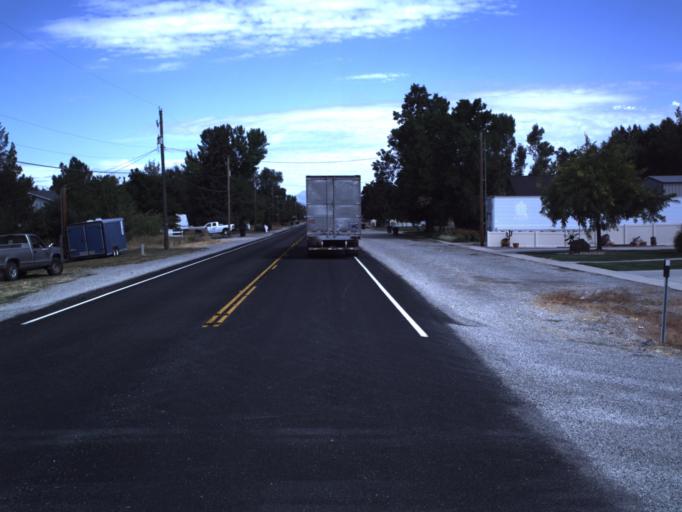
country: US
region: Utah
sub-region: Box Elder County
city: Honeyville
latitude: 41.6103
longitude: -112.1271
